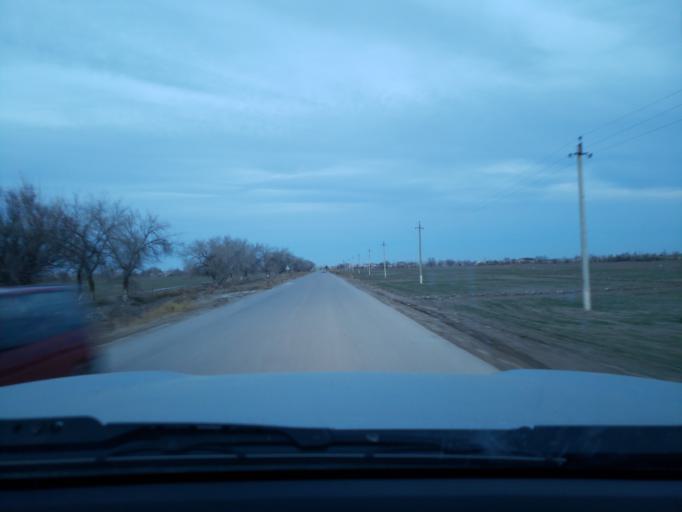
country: TM
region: Dasoguz
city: Tagta
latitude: 41.6261
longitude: 60.0628
